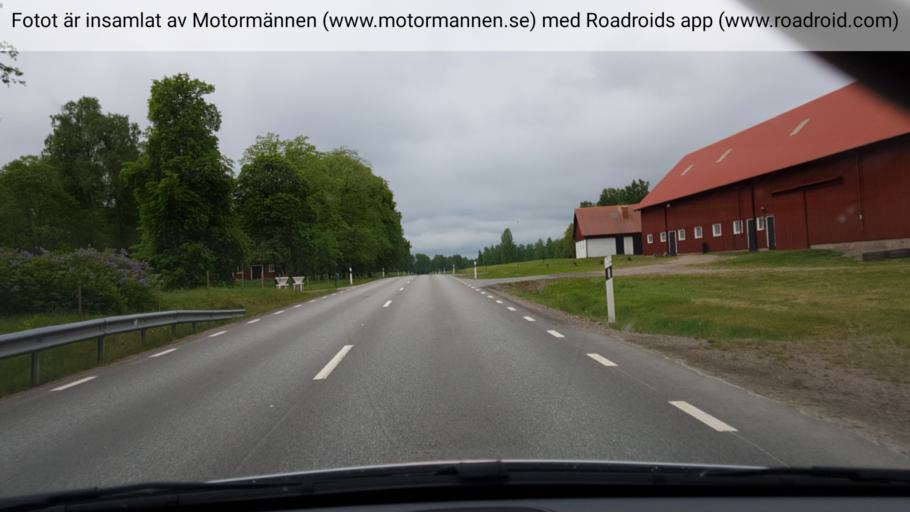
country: SE
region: Joenkoeping
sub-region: Mullsjo Kommun
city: Mullsjoe
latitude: 57.8476
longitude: 13.8542
